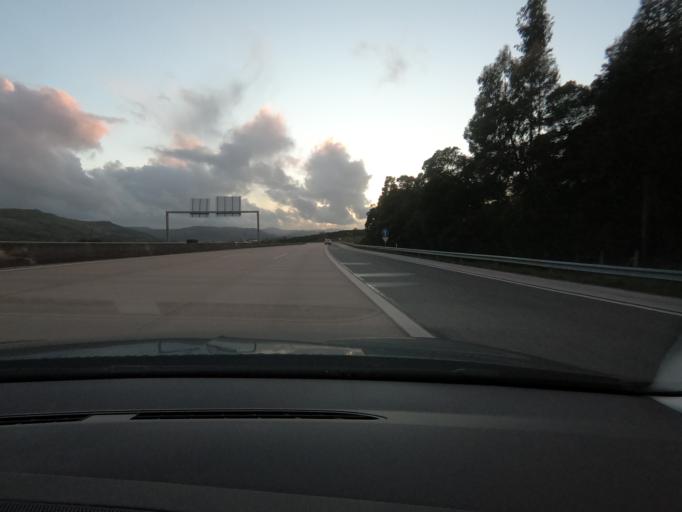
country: PT
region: Lisbon
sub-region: Vila Franca de Xira
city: Vialonga
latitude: 38.9079
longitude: -9.0774
